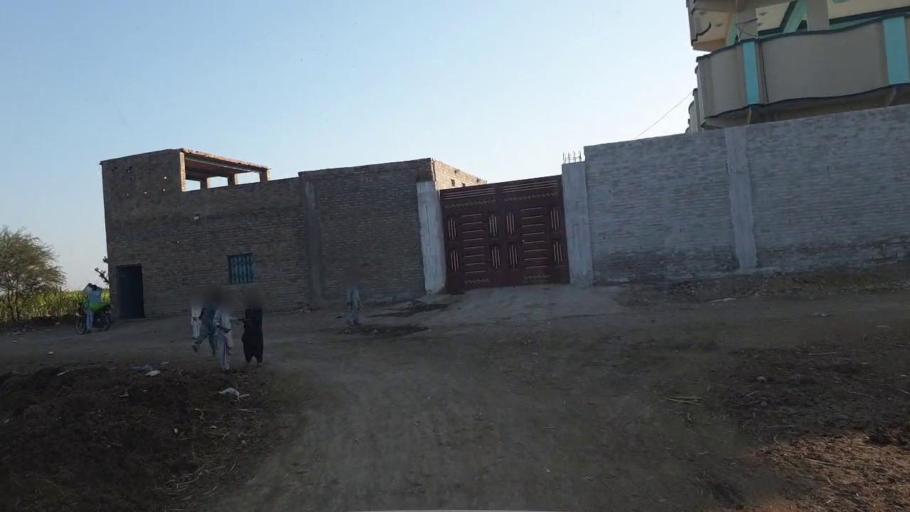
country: PK
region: Sindh
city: Tando Allahyar
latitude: 25.3758
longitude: 68.7051
